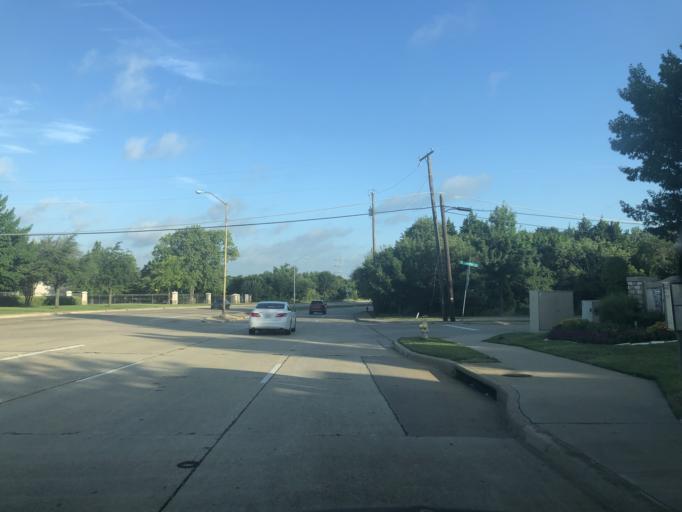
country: US
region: Texas
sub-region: Dallas County
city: Duncanville
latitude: 32.6667
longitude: -96.9449
